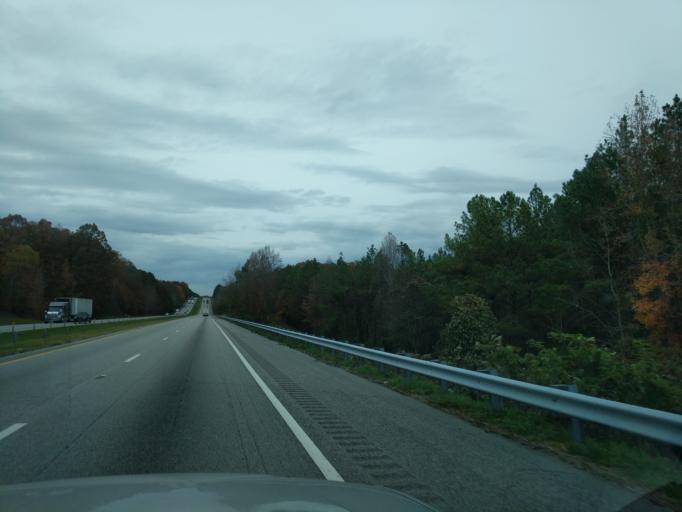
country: US
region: South Carolina
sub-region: Laurens County
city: Clinton
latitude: 34.5642
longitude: -81.8912
